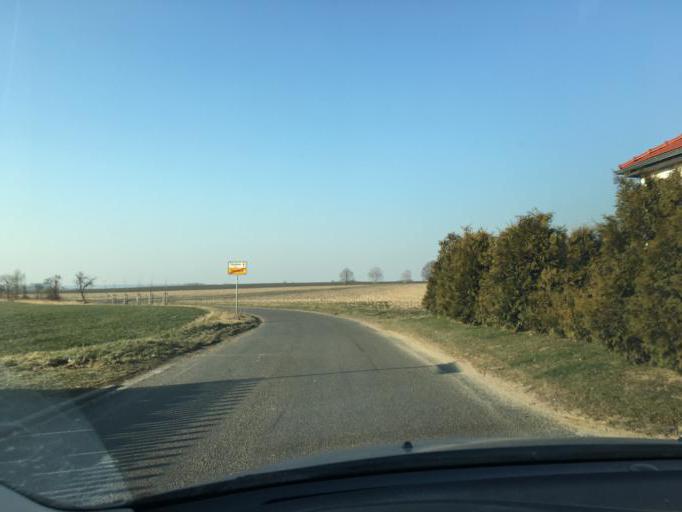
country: DE
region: Saxony
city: Otterwisch
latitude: 51.1726
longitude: 12.5956
